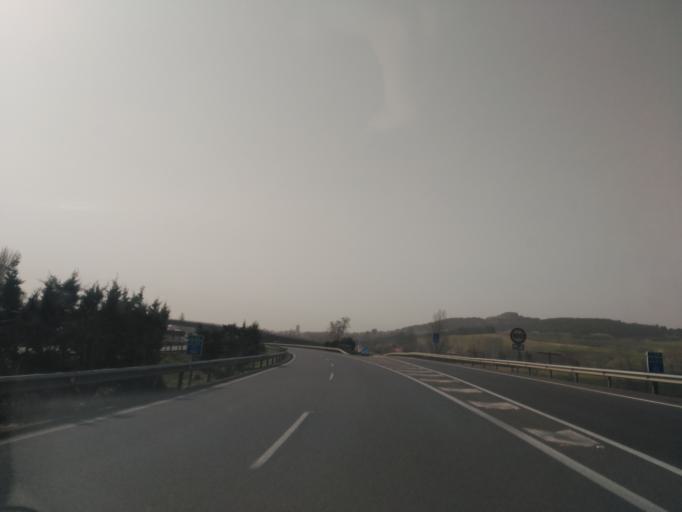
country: ES
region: Castille and Leon
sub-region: Provincia de Palencia
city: Duenas
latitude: 41.8899
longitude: -4.5290
